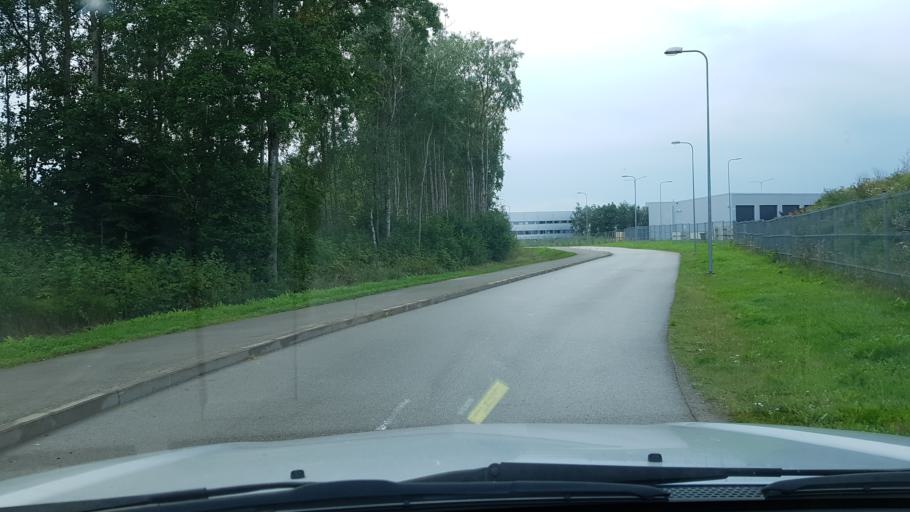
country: EE
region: Harju
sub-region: Rae vald
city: Jueri
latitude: 59.3599
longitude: 24.9344
